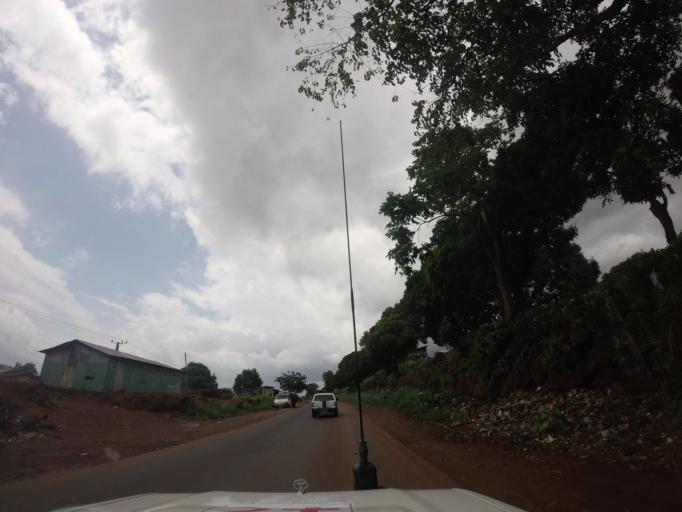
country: SL
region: Western Area
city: Waterloo
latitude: 8.3656
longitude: -13.0879
